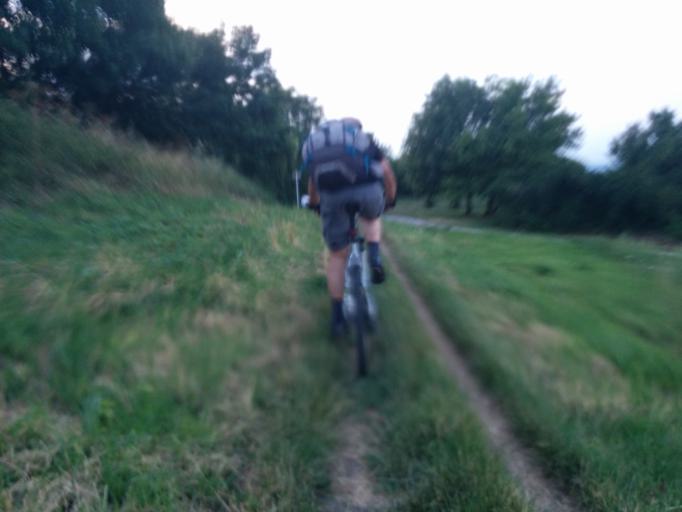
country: AT
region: Lower Austria
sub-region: Politischer Bezirk Modling
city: Neu-Guntramsdorf
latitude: 48.0662
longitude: 16.3009
